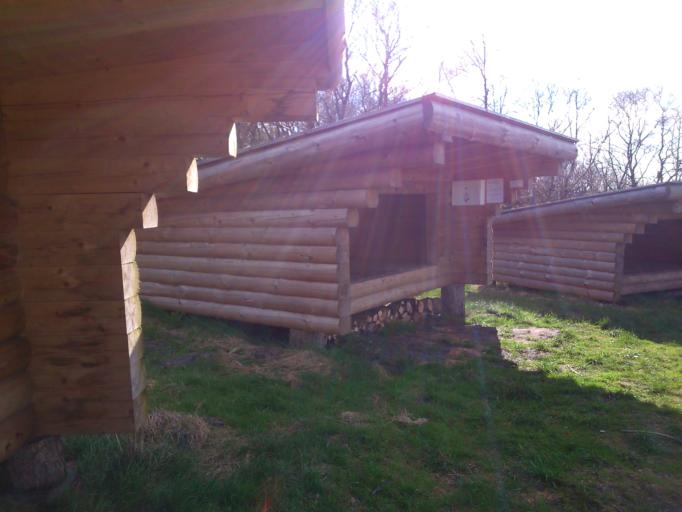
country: DK
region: Central Jutland
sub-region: Ringkobing-Skjern Kommune
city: Ringkobing
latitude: 56.1359
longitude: 8.3733
